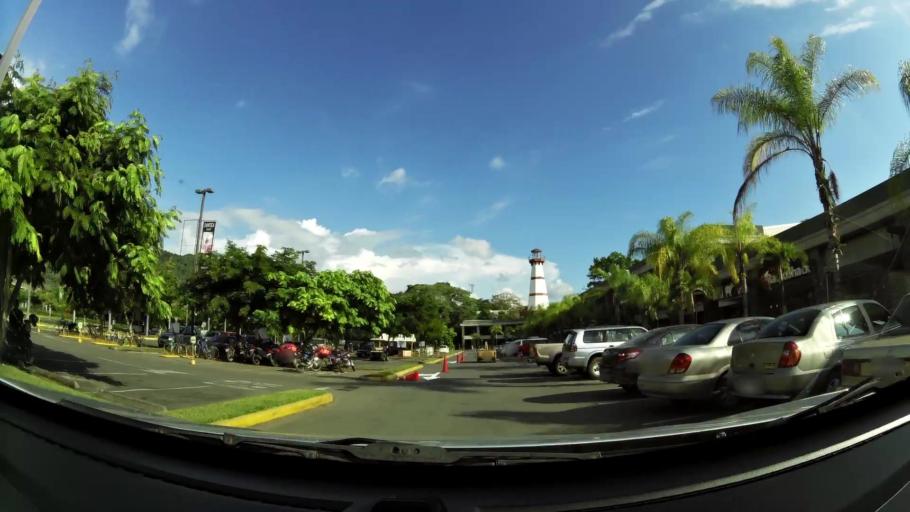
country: CR
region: Puntarenas
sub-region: Canton de Garabito
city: Jaco
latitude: 9.6616
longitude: -84.6392
